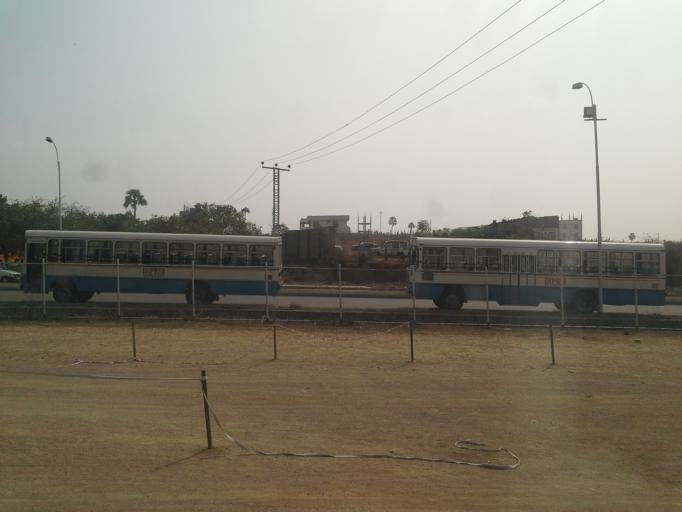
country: IN
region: Telangana
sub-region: Rangareddi
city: Lal Bahadur Nagar
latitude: 17.3088
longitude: 78.6812
